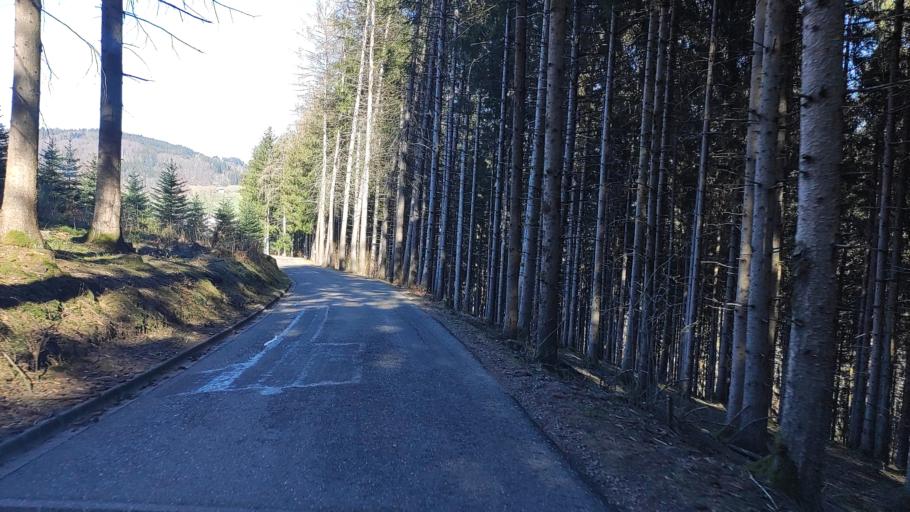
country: DE
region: Baden-Wuerttemberg
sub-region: Freiburg Region
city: Elzach
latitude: 48.1853
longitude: 8.0306
